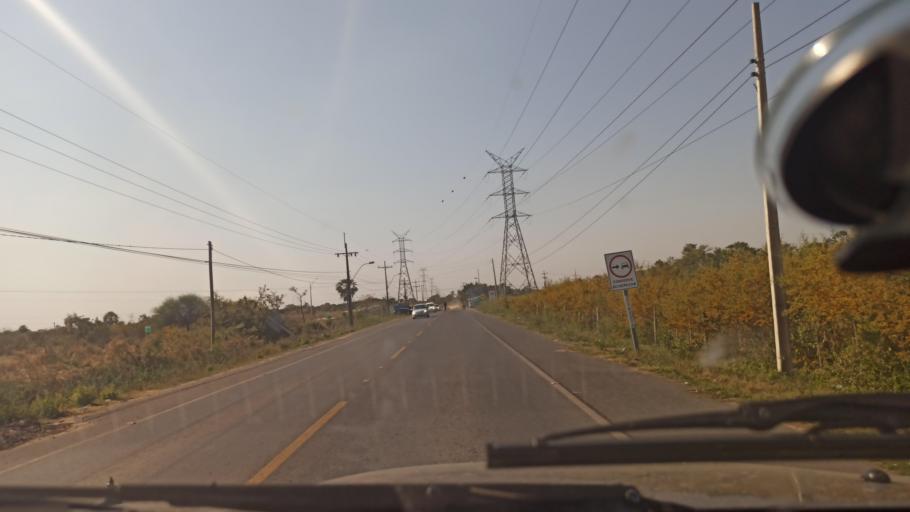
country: PY
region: Presidente Hayes
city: Nanawa
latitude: -25.2462
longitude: -57.6663
